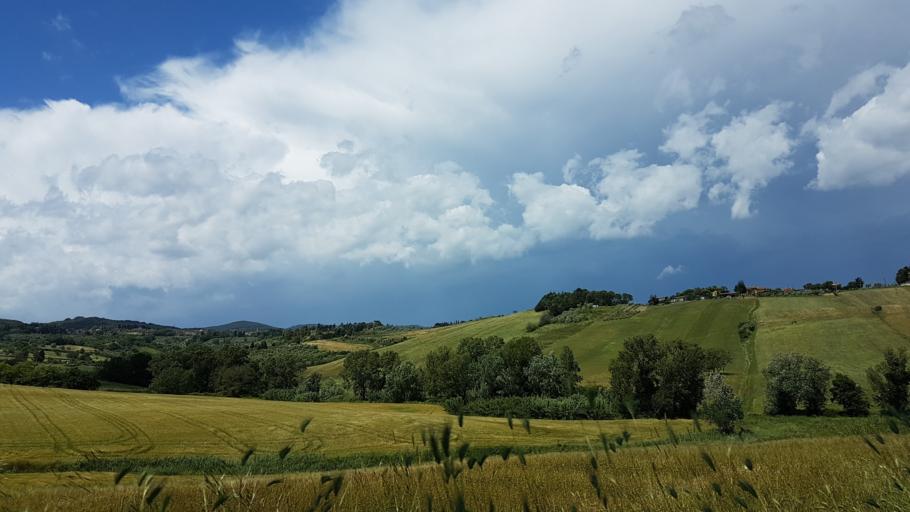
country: IT
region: Tuscany
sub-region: Provincia di Livorno
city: Rosignano Marittimo
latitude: 43.4256
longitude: 10.4781
